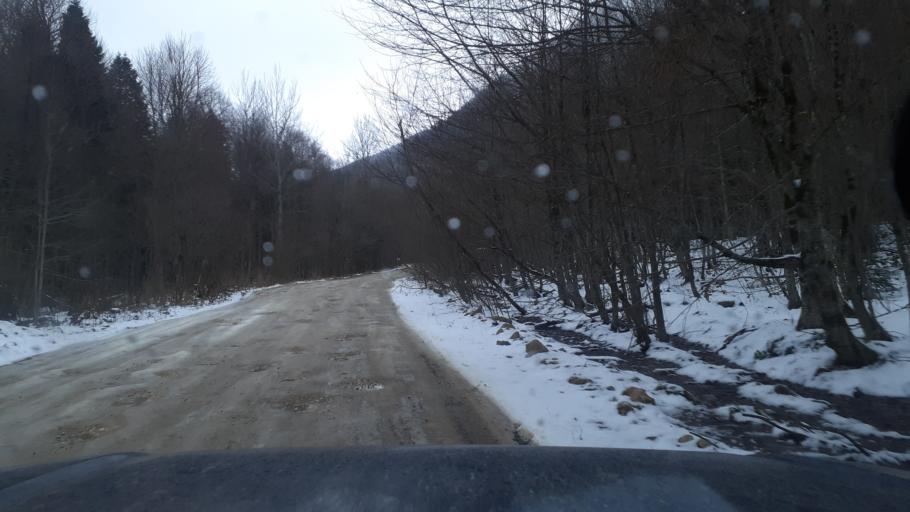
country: RU
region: Krasnodarskiy
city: Neftegorsk
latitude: 44.0761
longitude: 39.8056
